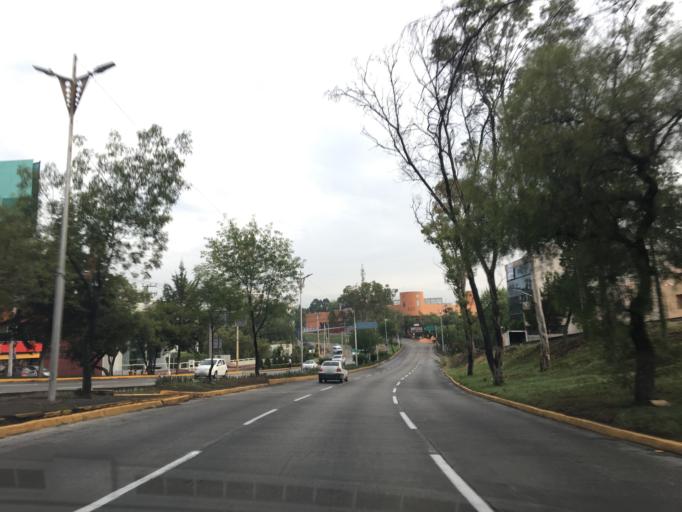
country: MX
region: Mexico
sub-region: Naucalpan de Juarez
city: Ejido del Tejocote
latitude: 19.5092
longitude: -99.2612
